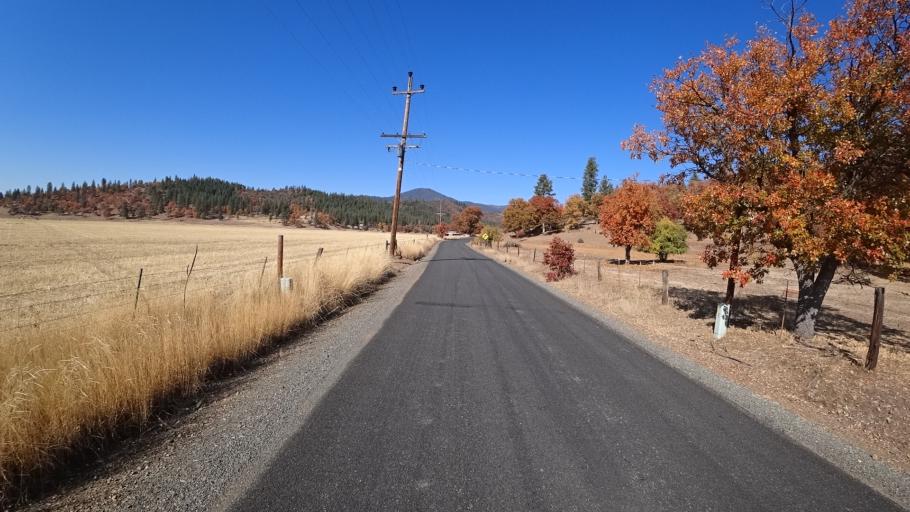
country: US
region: California
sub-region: Siskiyou County
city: Yreka
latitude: 41.6300
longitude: -122.8735
